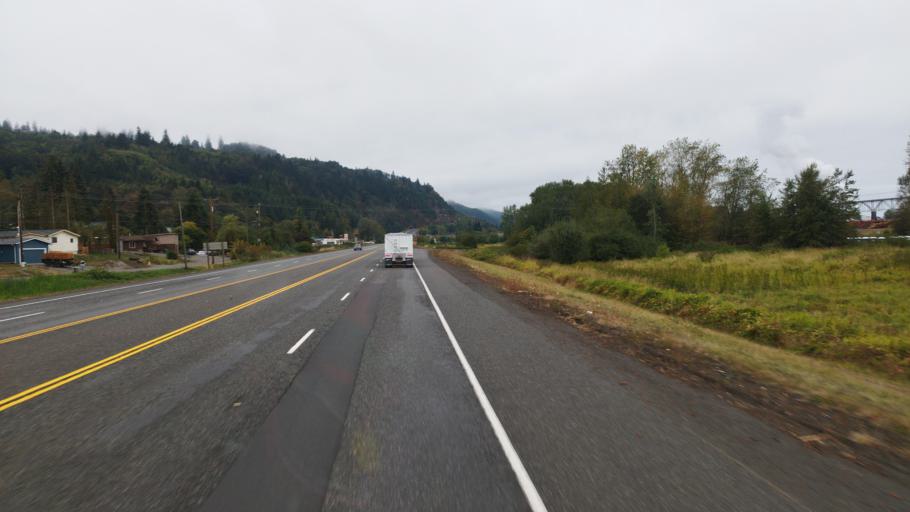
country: US
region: Oregon
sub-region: Columbia County
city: Rainier
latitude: 46.0944
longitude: -122.9562
